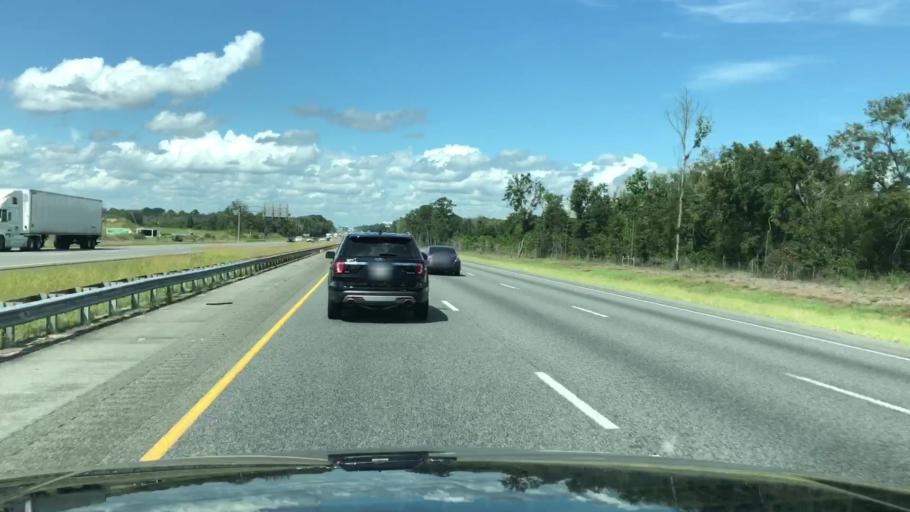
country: US
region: Georgia
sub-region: Lowndes County
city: Valdosta
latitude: 30.7874
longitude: -83.2994
